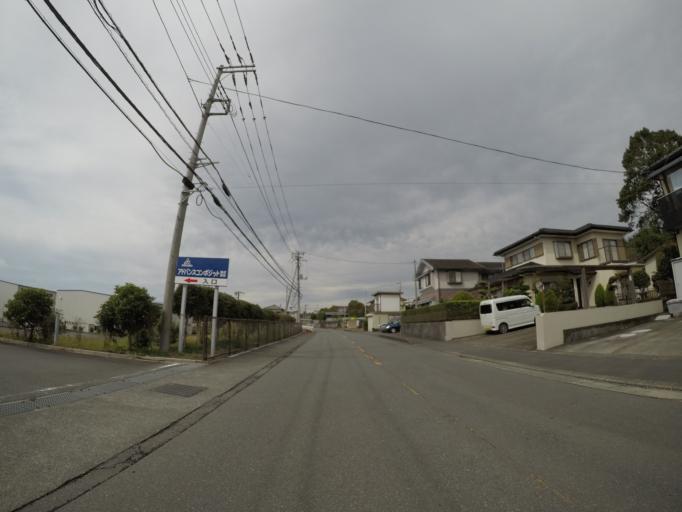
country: JP
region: Shizuoka
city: Fuji
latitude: 35.2198
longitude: 138.6829
